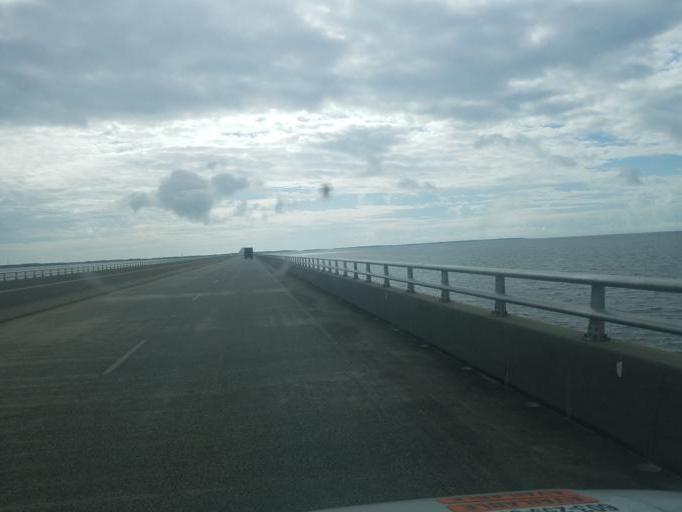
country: US
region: North Carolina
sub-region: Dare County
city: Manteo
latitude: 35.8870
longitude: -75.7333
